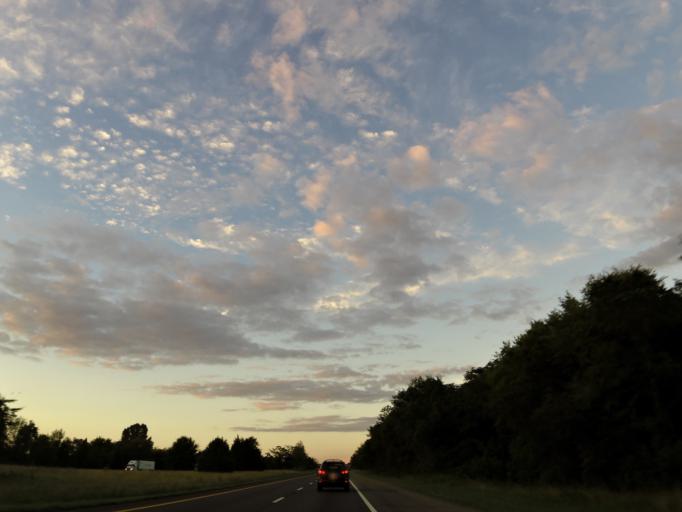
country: US
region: Tennessee
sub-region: Monroe County
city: Sweetwater
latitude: 35.6609
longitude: -84.4559
